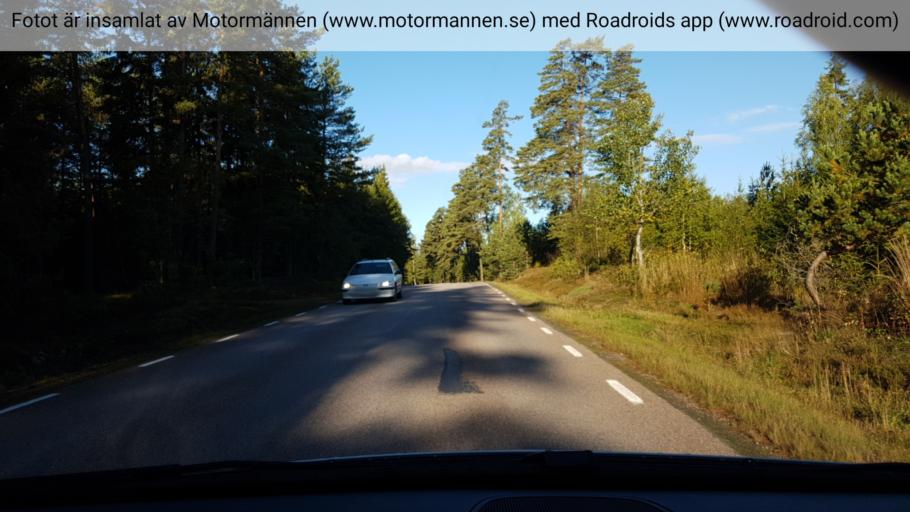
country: SE
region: Vaestra Goetaland
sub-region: Gotene Kommun
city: Goetene
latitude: 58.5447
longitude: 13.6778
